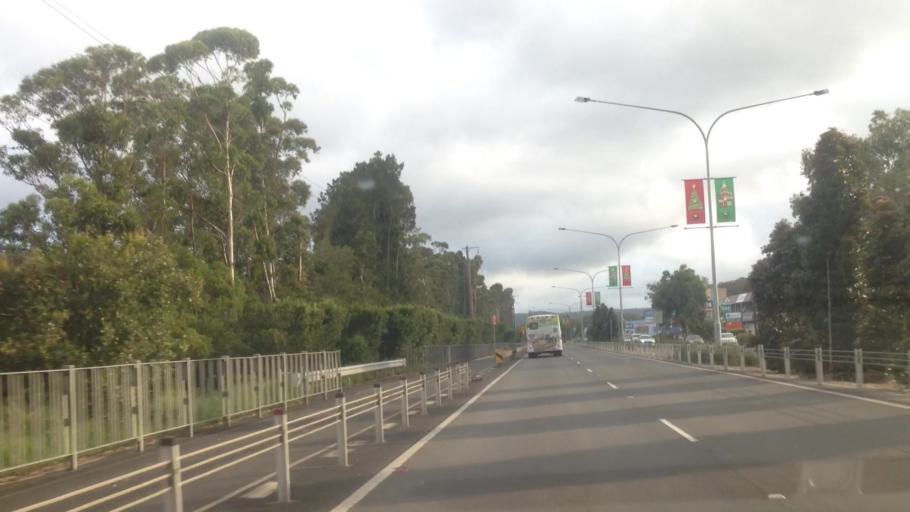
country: AU
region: New South Wales
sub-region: Wyong Shire
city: Chittaway Bay
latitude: -33.3015
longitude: 151.4212
